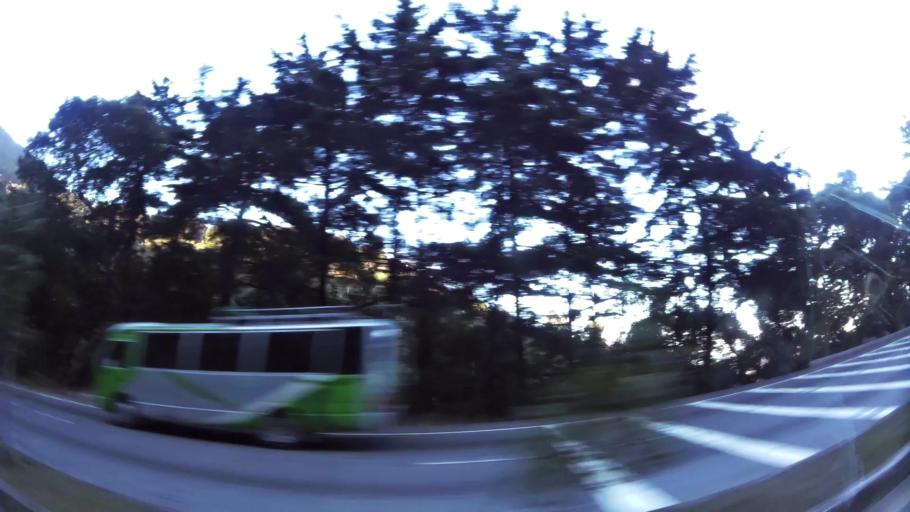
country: GT
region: Guatemala
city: Mixco
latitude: 14.6088
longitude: -90.6249
